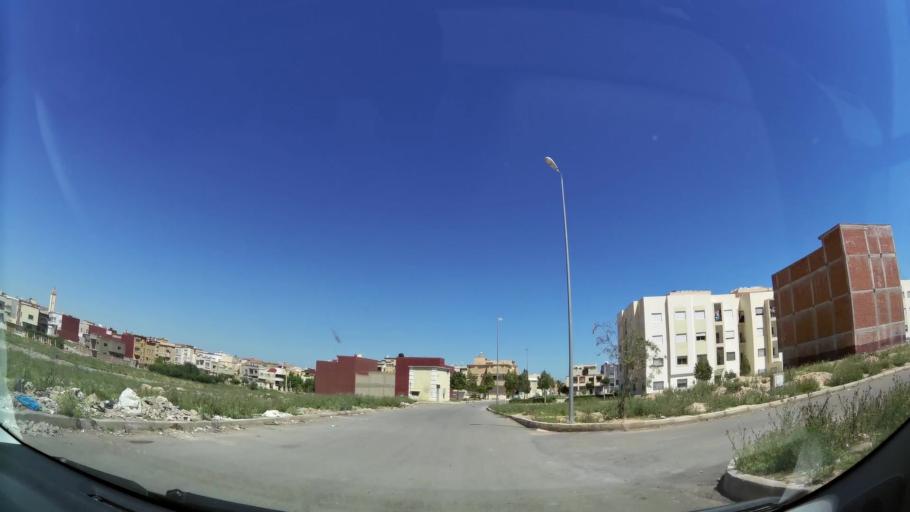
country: MA
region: Oriental
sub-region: Oujda-Angad
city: Oujda
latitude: 34.6549
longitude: -1.8829
